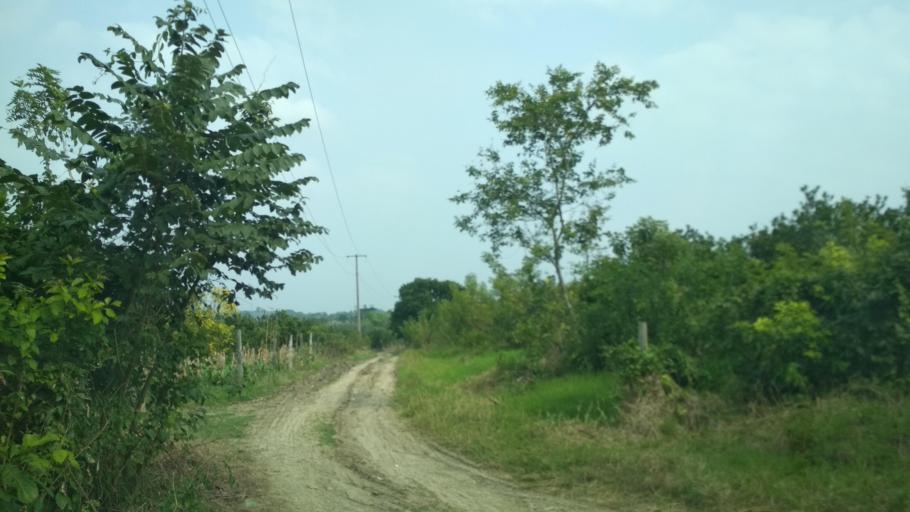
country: MM
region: Kayah
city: Loikaw
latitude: 20.2060
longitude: 97.3174
